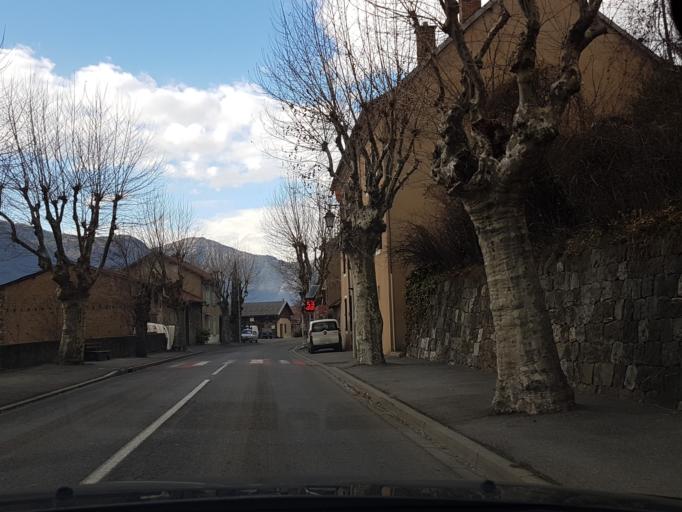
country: FR
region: Provence-Alpes-Cote d'Azur
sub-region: Departement des Hautes-Alpes
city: La Batie-Neuve
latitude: 44.4681
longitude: 6.1712
